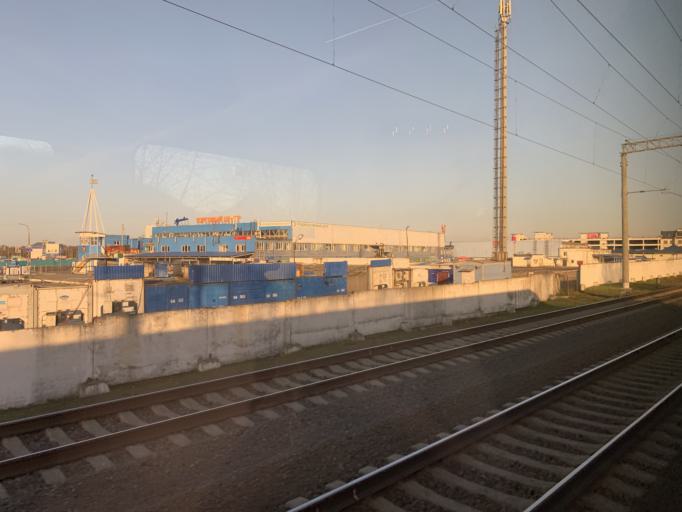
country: BY
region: Minsk
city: Zhdanovichy
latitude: 53.9403
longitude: 27.4383
